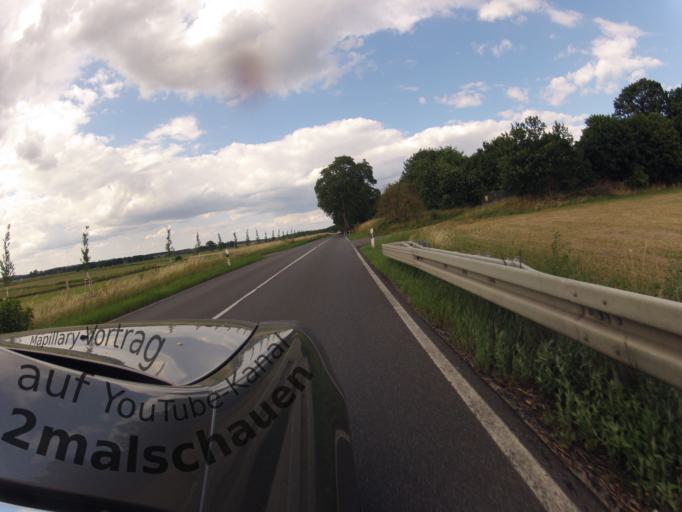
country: DE
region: Mecklenburg-Vorpommern
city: Seebad Heringsdorf
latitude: 53.9009
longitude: 14.1473
